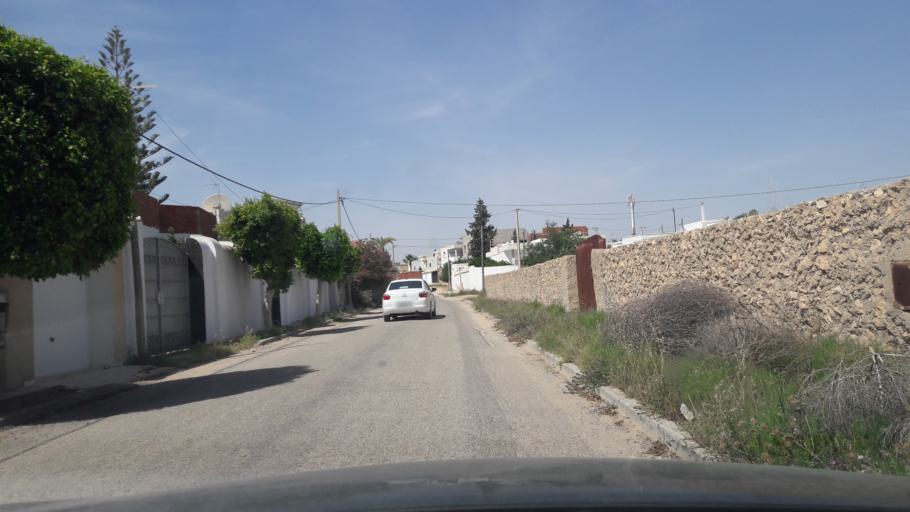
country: TN
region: Safaqis
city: Sfax
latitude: 34.7876
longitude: 10.7530
